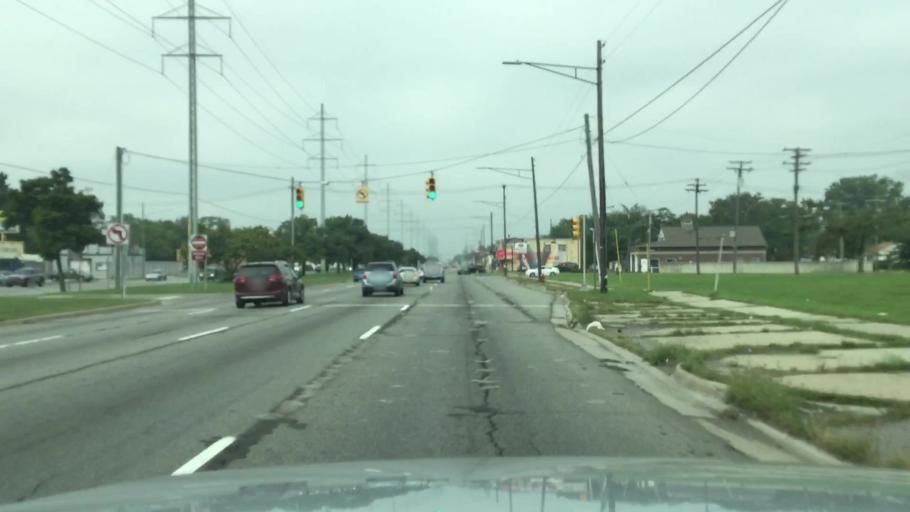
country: US
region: Michigan
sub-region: Macomb County
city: Eastpointe
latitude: 42.4494
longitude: -82.9939
